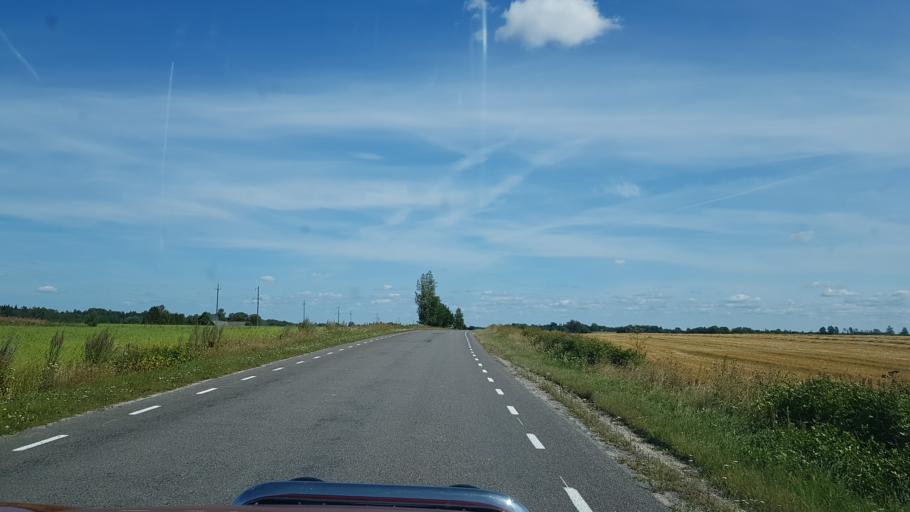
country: EE
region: Jaervamaa
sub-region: Jaerva-Jaani vald
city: Jarva-Jaani
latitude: 59.0426
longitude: 25.9793
